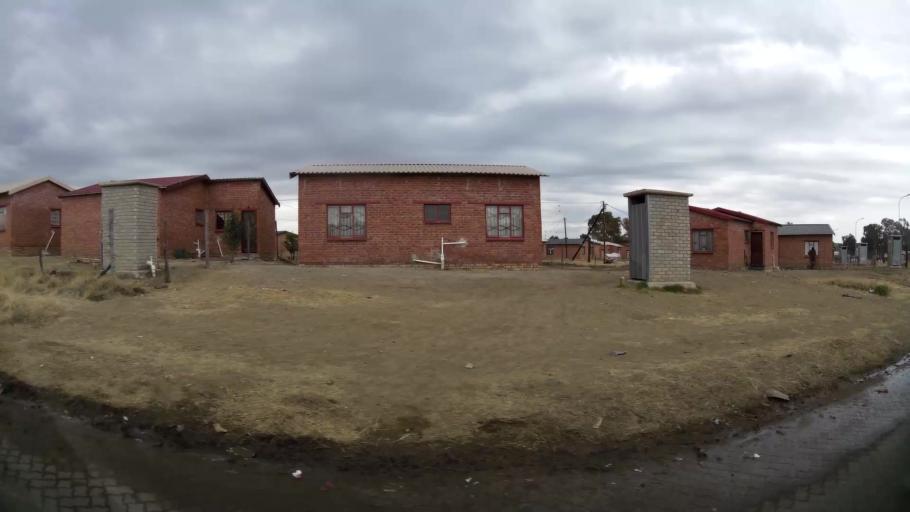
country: ZA
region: Orange Free State
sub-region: Fezile Dabi District Municipality
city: Kroonstad
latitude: -27.6530
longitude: 27.2227
